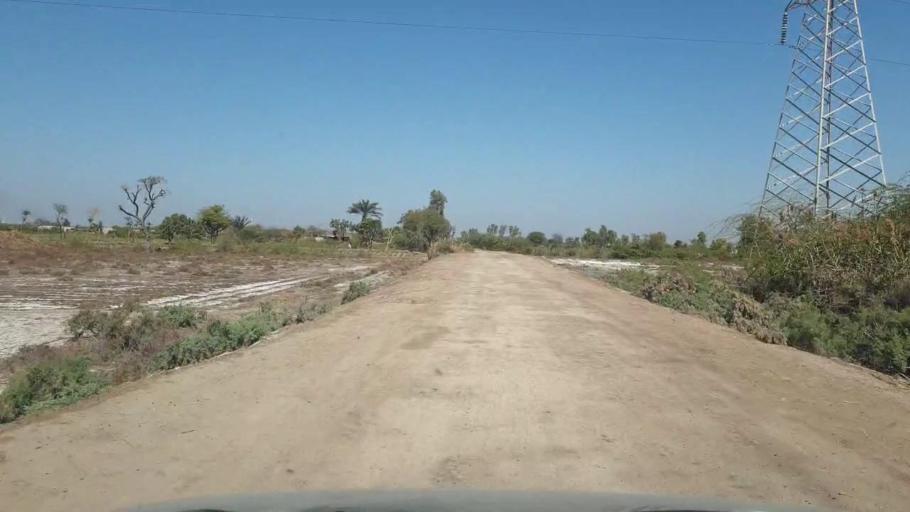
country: PK
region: Sindh
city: Mirwah Gorchani
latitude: 25.3133
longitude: 69.1283
